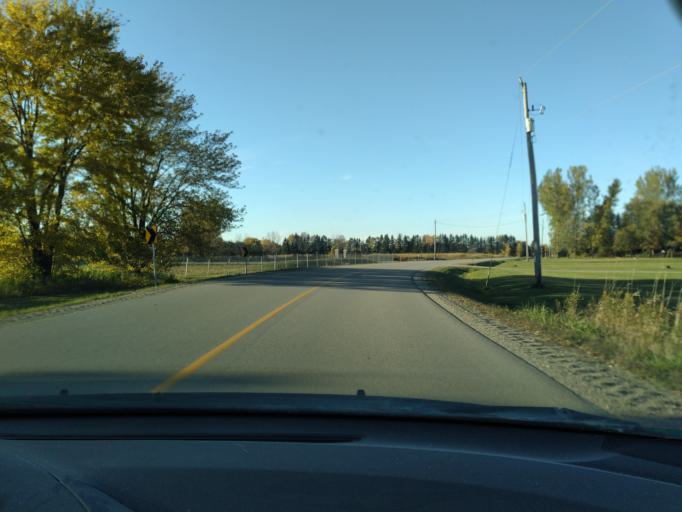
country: CA
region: Ontario
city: Bradford West Gwillimbury
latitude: 44.0204
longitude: -79.7273
